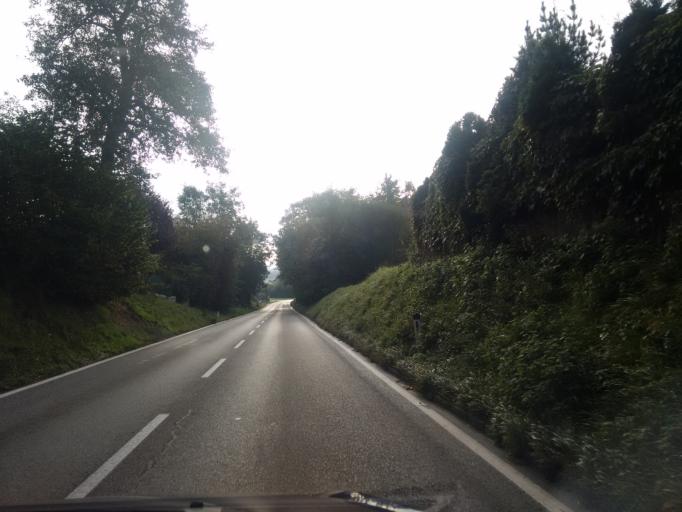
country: AT
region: Upper Austria
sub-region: Wels-Land
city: Gunskirchen
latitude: 48.1811
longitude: 13.9774
